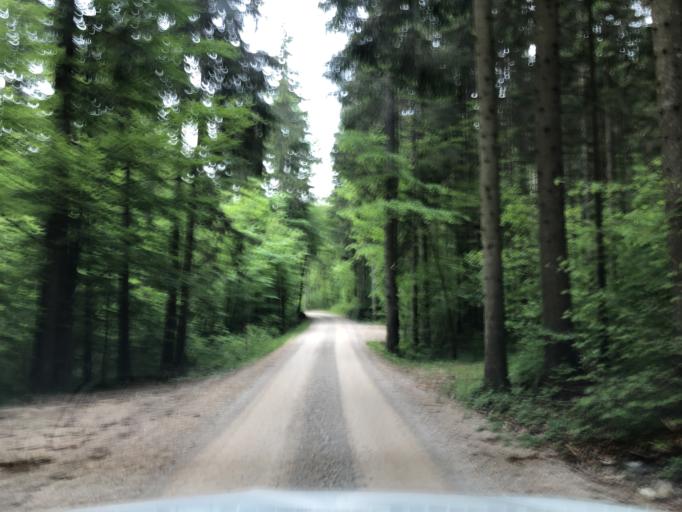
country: SI
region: Bloke
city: Nova Vas
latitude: 45.7515
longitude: 14.4632
